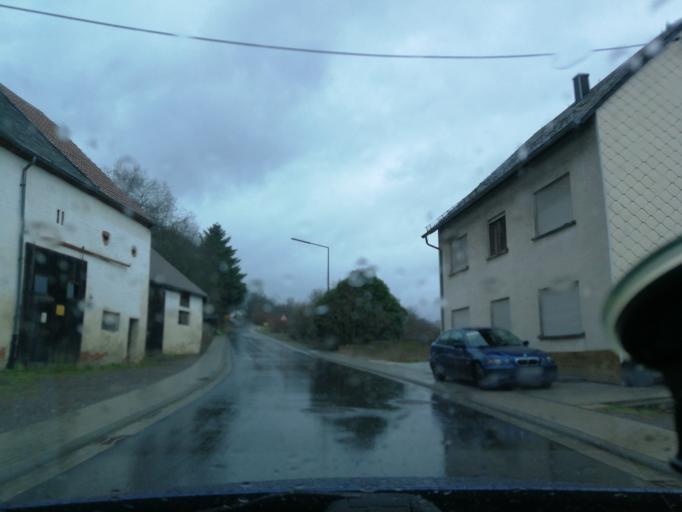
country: DE
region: Rheinland-Pfalz
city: Deuselbach
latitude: 49.7538
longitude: 7.0507
